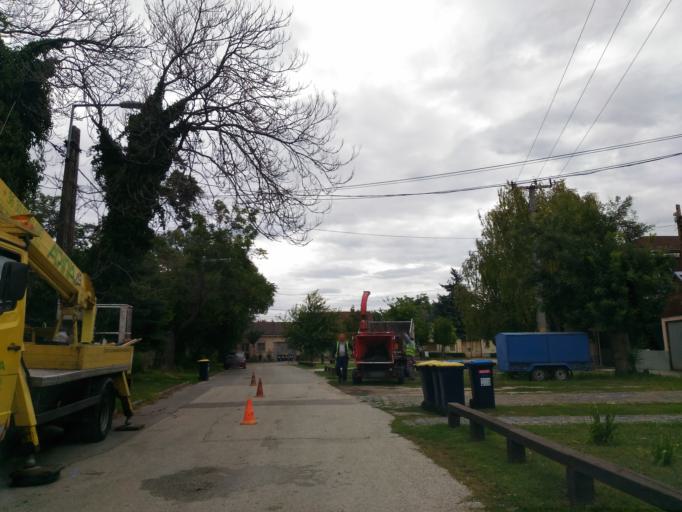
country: HU
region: Pest
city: Halasztelek
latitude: 47.3913
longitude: 18.9850
